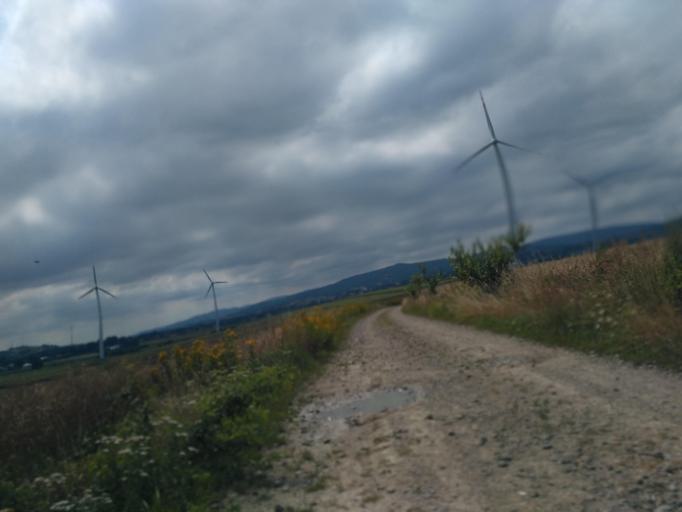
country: PL
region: Subcarpathian Voivodeship
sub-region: Powiat krosnienski
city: Rymanow
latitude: 49.6041
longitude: 21.8473
